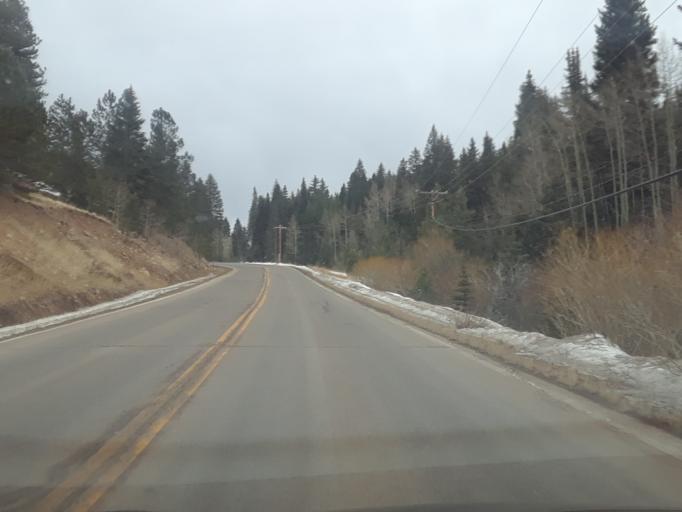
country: US
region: Colorado
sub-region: Boulder County
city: Coal Creek
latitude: 39.8245
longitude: -105.4106
